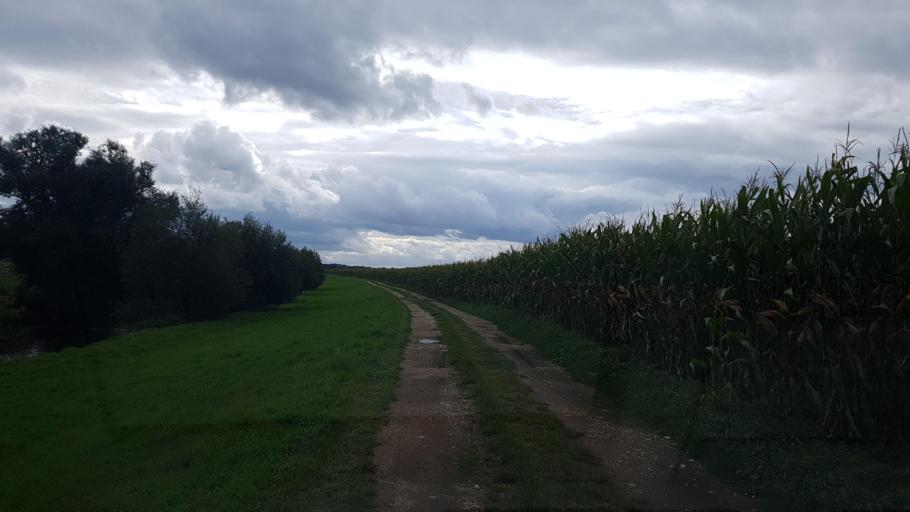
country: DE
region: Saxony
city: Pegau
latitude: 51.1483
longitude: 12.2570
